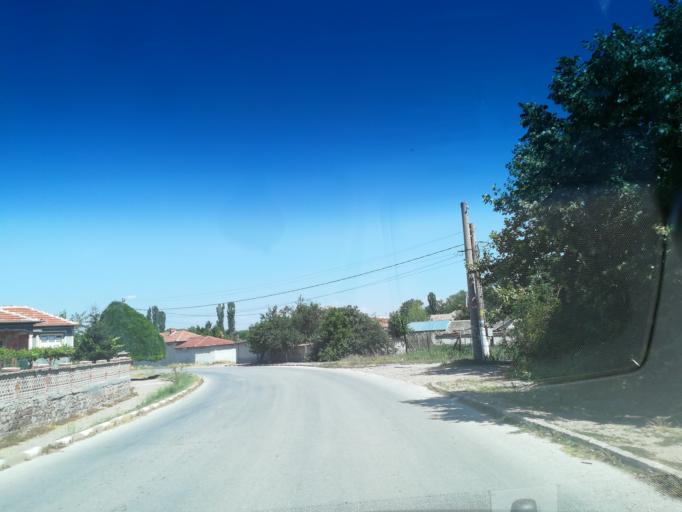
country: BG
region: Plovdiv
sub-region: Obshtina Sadovo
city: Sadovo
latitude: 42.0271
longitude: 25.1102
